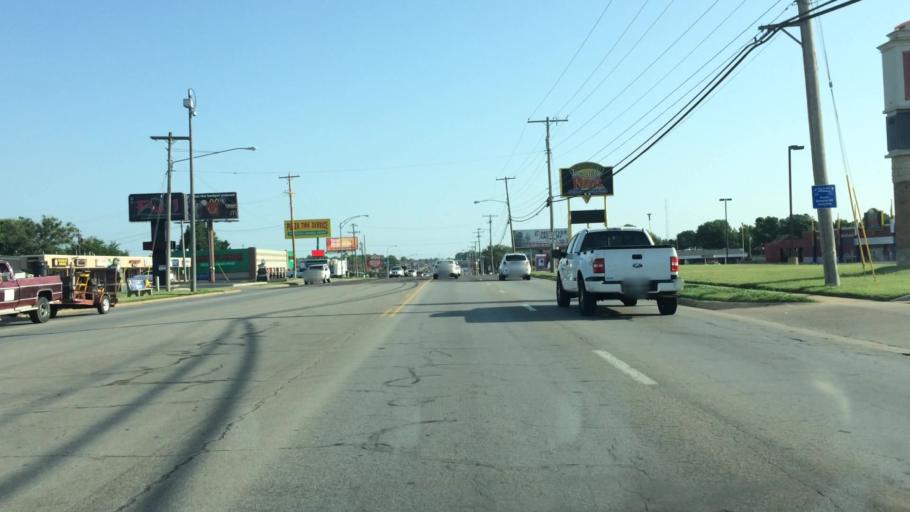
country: US
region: Missouri
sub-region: Greene County
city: Springfield
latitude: 37.1609
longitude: -93.2954
